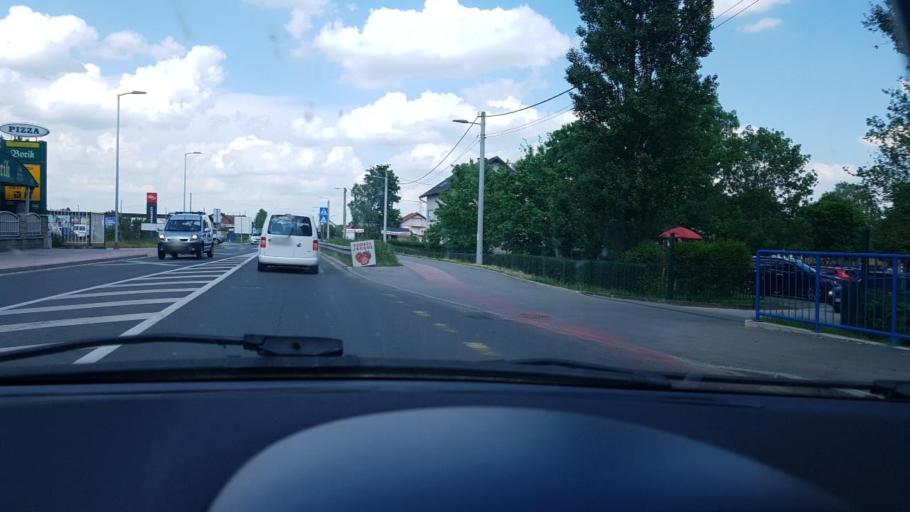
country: HR
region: Grad Zagreb
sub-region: Sesvete
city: Sesvete
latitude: 45.8651
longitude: 16.1550
